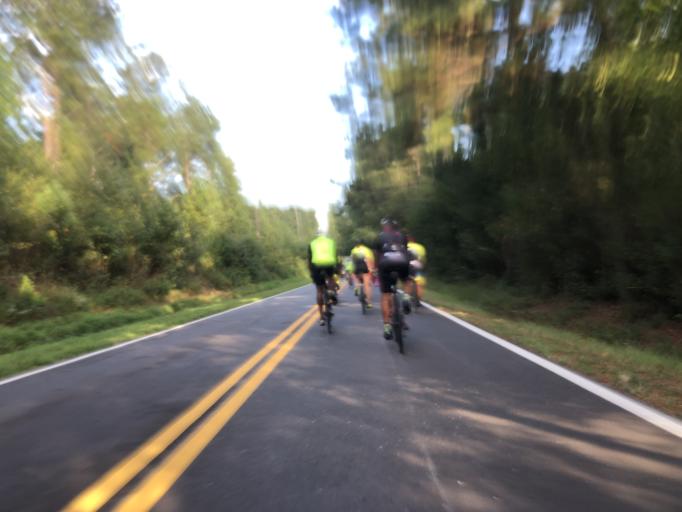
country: US
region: Georgia
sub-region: Fulton County
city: Palmetto
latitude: 33.5779
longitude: -84.6787
